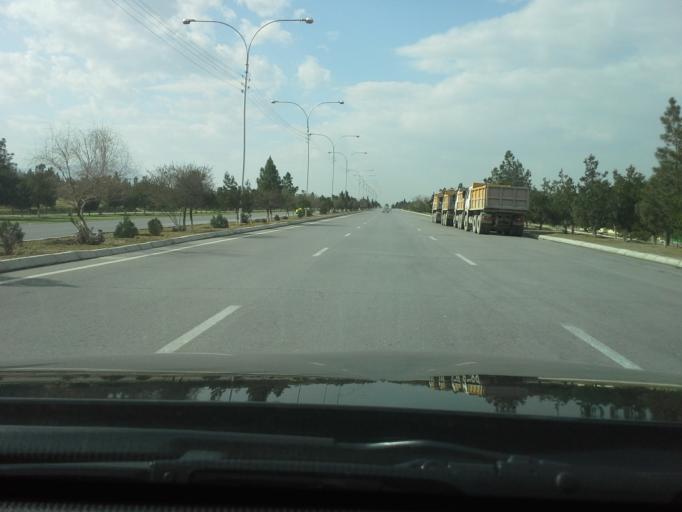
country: TM
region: Ahal
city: Ashgabat
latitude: 37.9663
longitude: 58.3051
